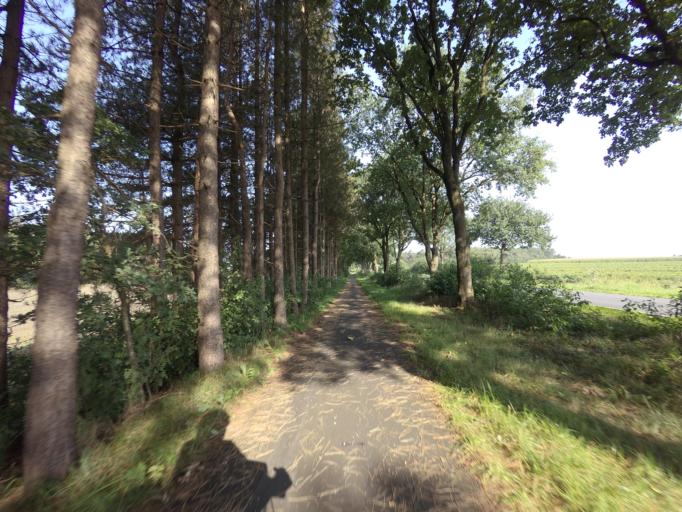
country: DE
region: Lower Saxony
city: Wielen
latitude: 52.5435
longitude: 6.6964
